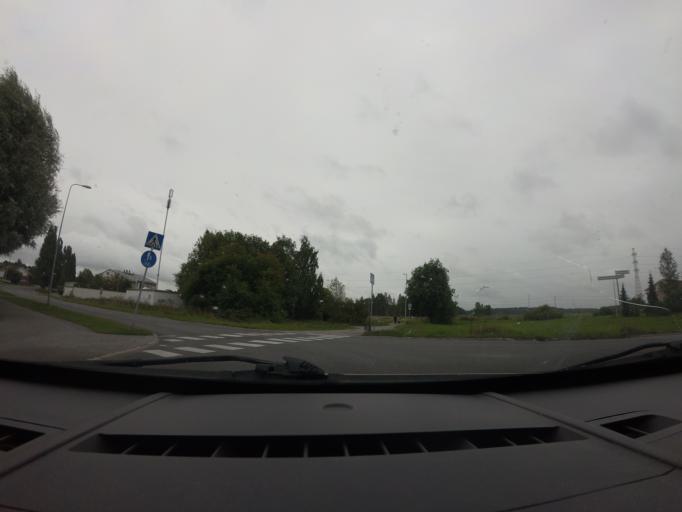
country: FI
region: Varsinais-Suomi
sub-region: Turku
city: Turku
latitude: 60.4129
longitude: 22.2894
